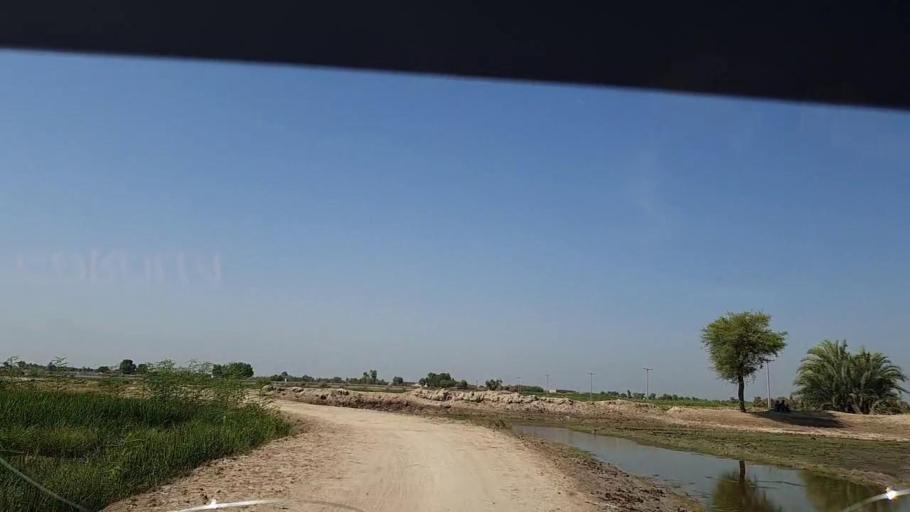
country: PK
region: Sindh
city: Tangwani
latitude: 28.3248
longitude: 69.0865
